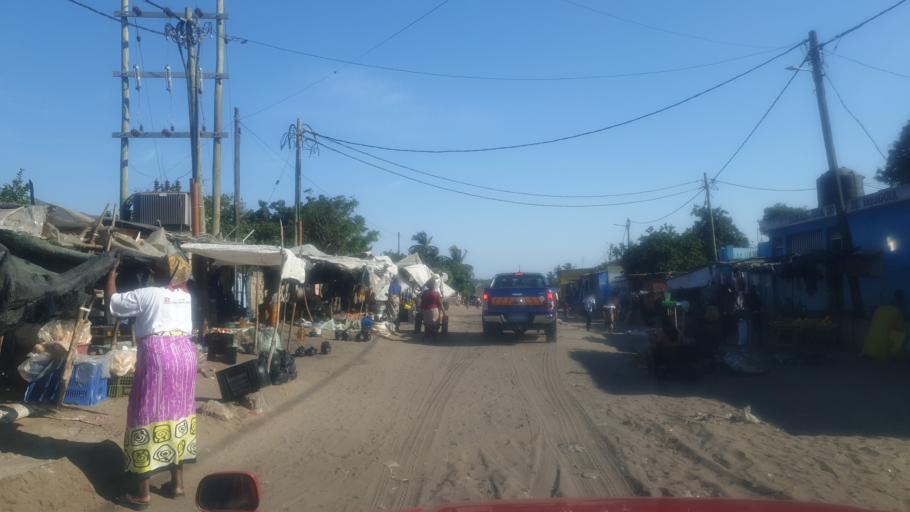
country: MZ
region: Maputo City
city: Maputo
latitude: -25.9190
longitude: 32.5572
